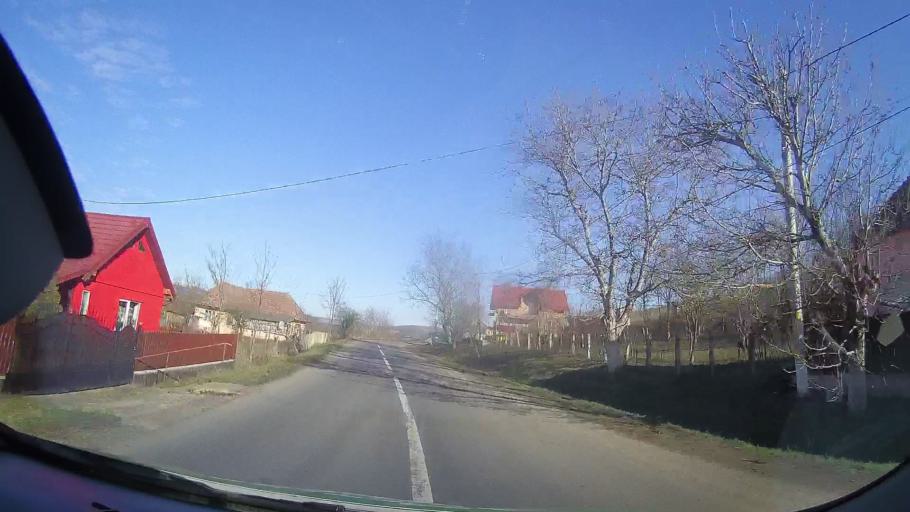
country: RO
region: Mures
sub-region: Comuna Band
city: Band
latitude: 46.5648
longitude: 24.3401
